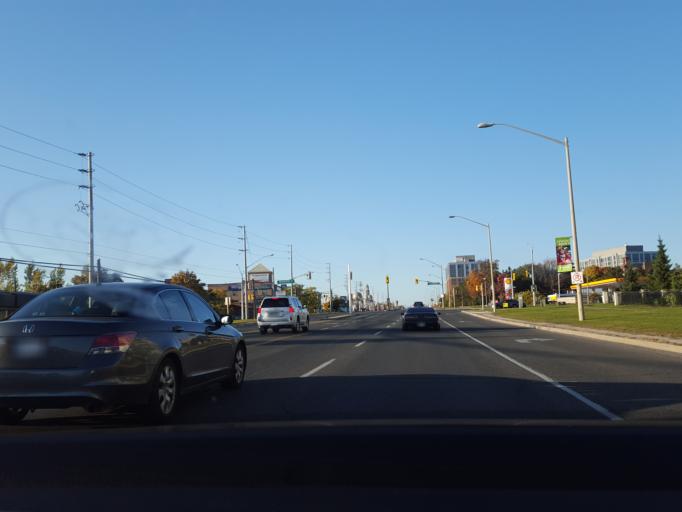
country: CA
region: Ontario
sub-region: York
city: Richmond Hill
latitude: 43.8975
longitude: -79.4432
